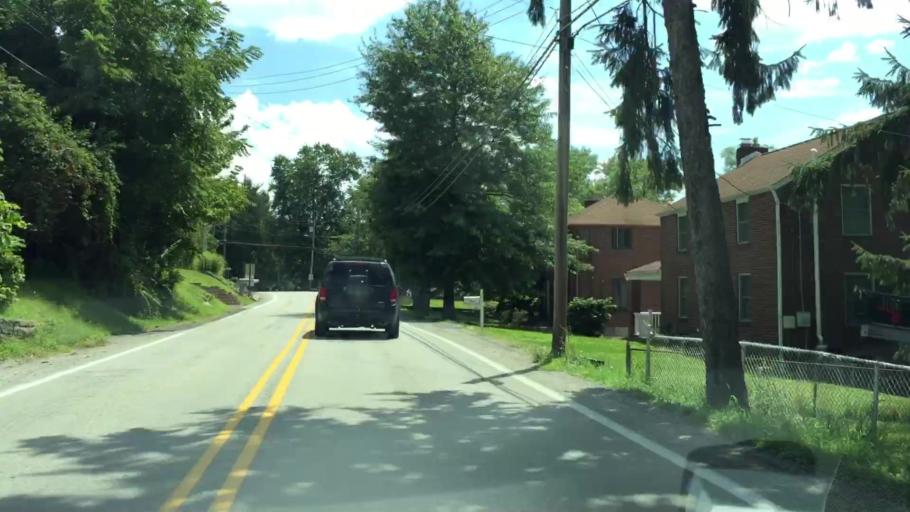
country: US
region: Pennsylvania
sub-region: Allegheny County
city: Bethel Park
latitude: 40.3122
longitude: -80.0357
